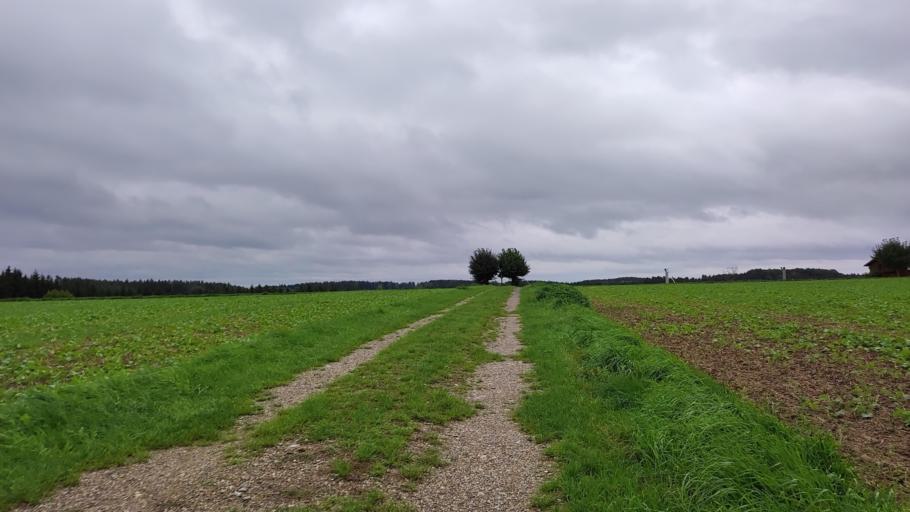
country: DE
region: Bavaria
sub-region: Swabia
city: Altenmunster
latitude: 48.4490
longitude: 10.6191
